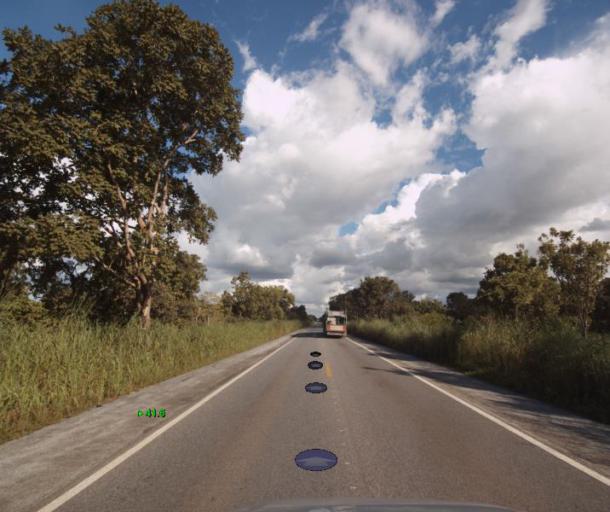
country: BR
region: Goias
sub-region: Porangatu
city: Porangatu
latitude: -13.1839
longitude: -49.1663
